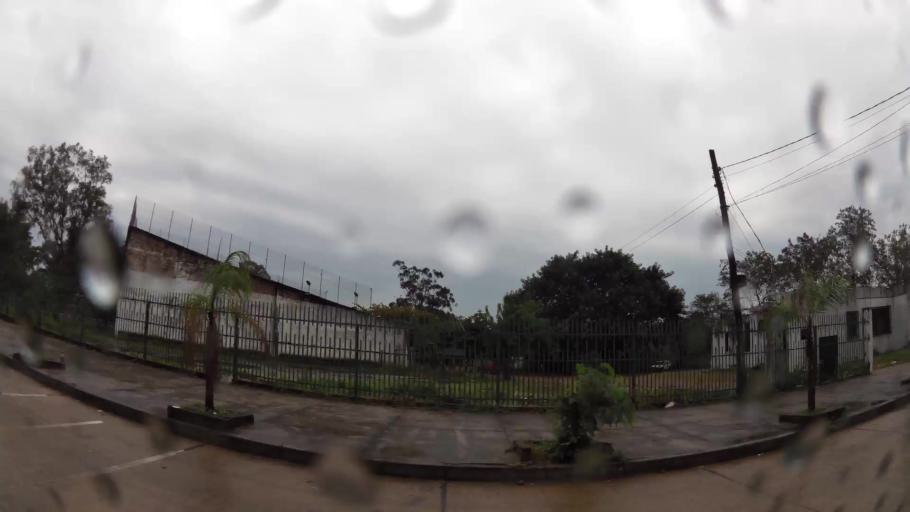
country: BO
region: Santa Cruz
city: Santa Cruz de la Sierra
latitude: -17.8119
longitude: -63.1959
